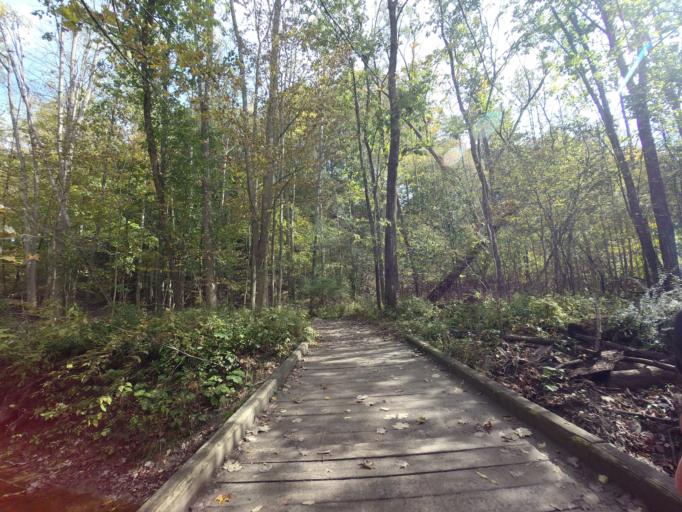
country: CA
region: Ontario
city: Ancaster
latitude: 43.2543
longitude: -79.9716
